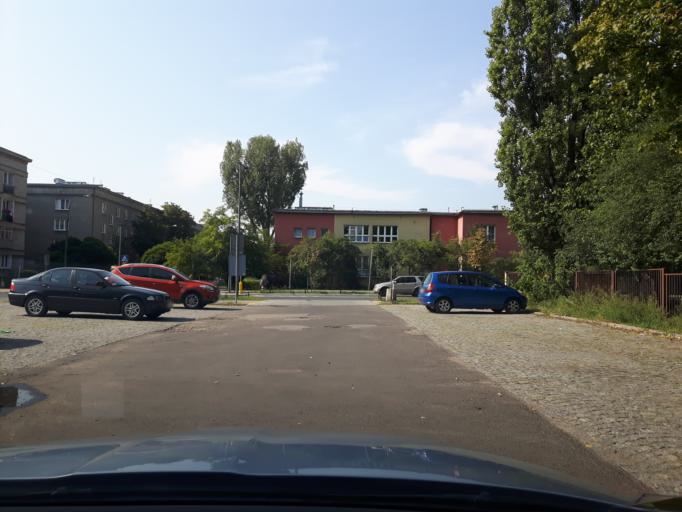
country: PL
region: Masovian Voivodeship
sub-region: Warszawa
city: Praga Polnoc
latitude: 52.2650
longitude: 21.0327
